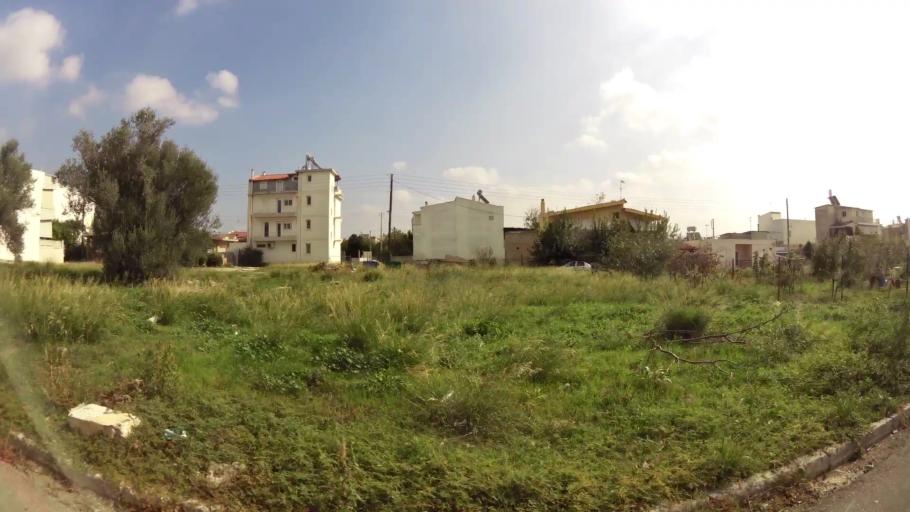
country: GR
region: Attica
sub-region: Nomarchia Dytikis Attikis
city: Zefyri
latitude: 38.0538
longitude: 23.7268
